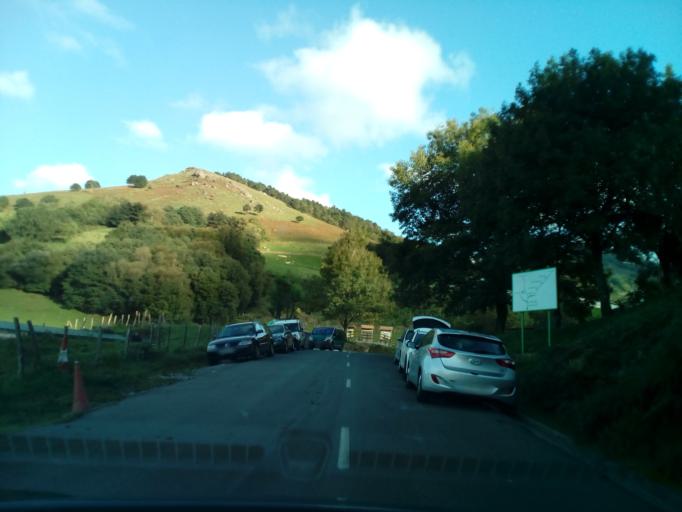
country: ES
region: Basque Country
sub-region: Provincia de Guipuzcoa
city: Urnieta
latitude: 43.2221
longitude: -1.9749
